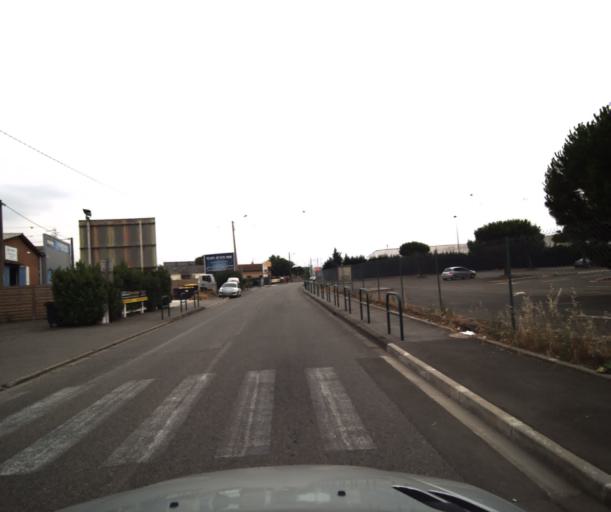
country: FR
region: Midi-Pyrenees
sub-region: Departement de la Haute-Garonne
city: Portet-sur-Garonne
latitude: 43.5375
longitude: 1.4034
